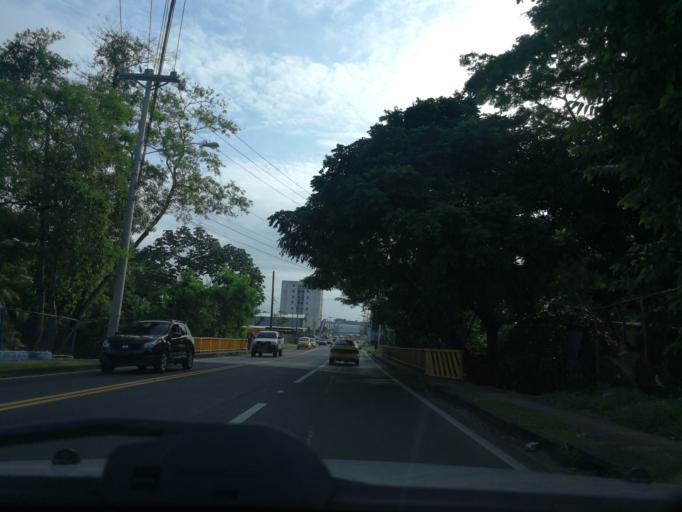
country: PA
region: Panama
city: Panama
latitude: 9.0197
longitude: -79.5001
